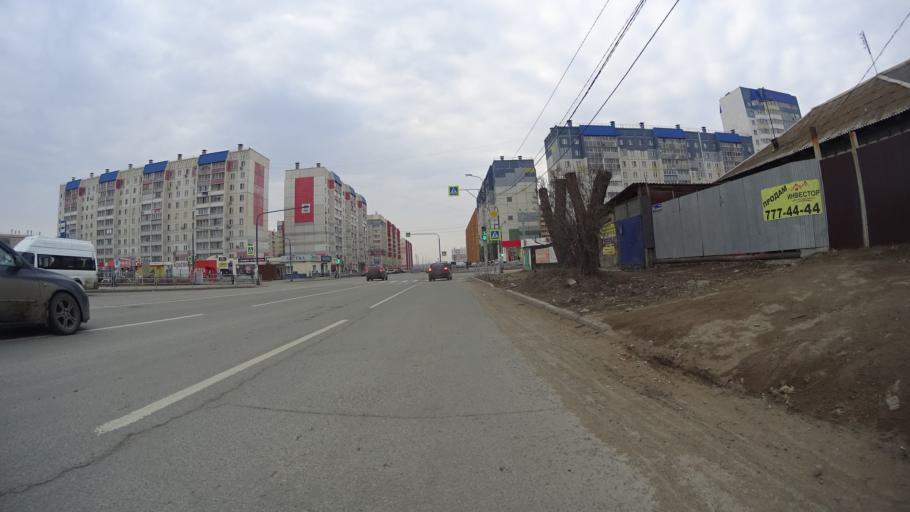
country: RU
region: Chelyabinsk
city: Zheleznodorozhnyy
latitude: 55.1663
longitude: 61.5222
